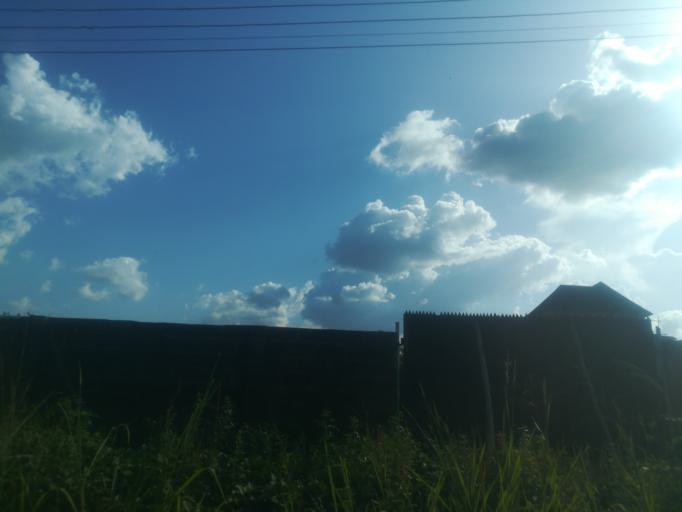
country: NG
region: Oyo
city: Ibadan
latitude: 7.4341
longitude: 3.9766
